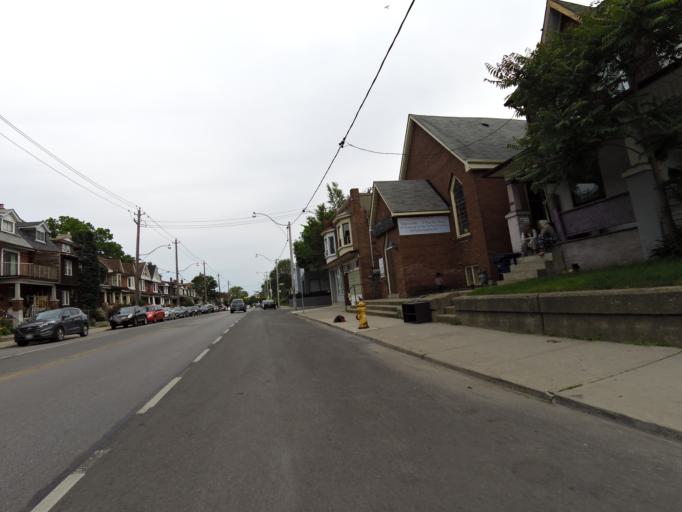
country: CA
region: Ontario
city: Toronto
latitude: 43.6786
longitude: -79.3397
